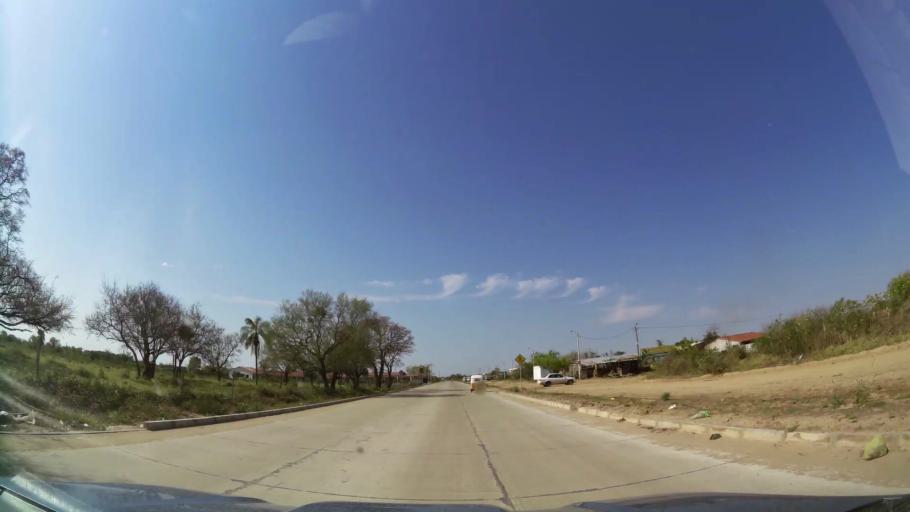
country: BO
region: Santa Cruz
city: Cotoca
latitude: -17.7182
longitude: -63.0729
